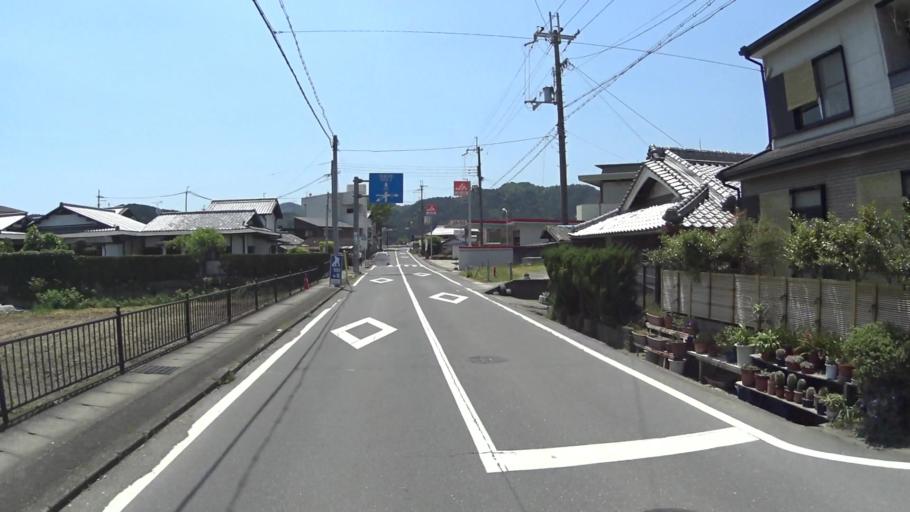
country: JP
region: Kyoto
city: Kameoka
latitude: 35.0729
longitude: 135.5386
